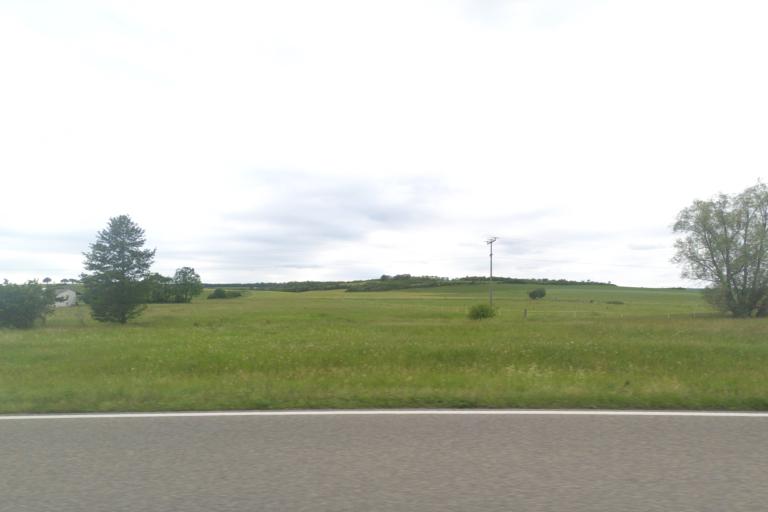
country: DE
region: Bavaria
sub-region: Regierungsbezirk Mittelfranken
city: Sugenheim
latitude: 49.5821
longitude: 10.4109
